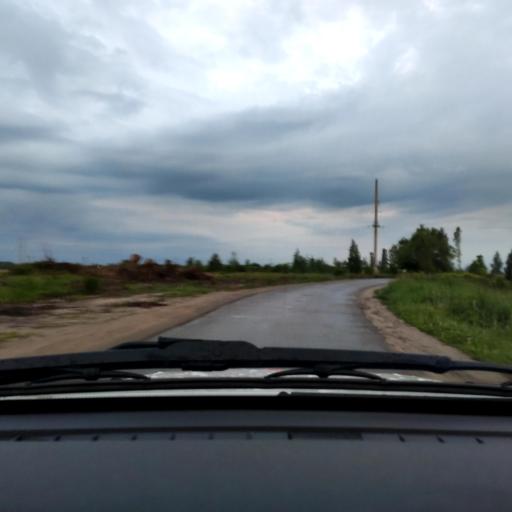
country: RU
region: Voronezj
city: Maslovka
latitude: 51.5163
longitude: 39.2268
